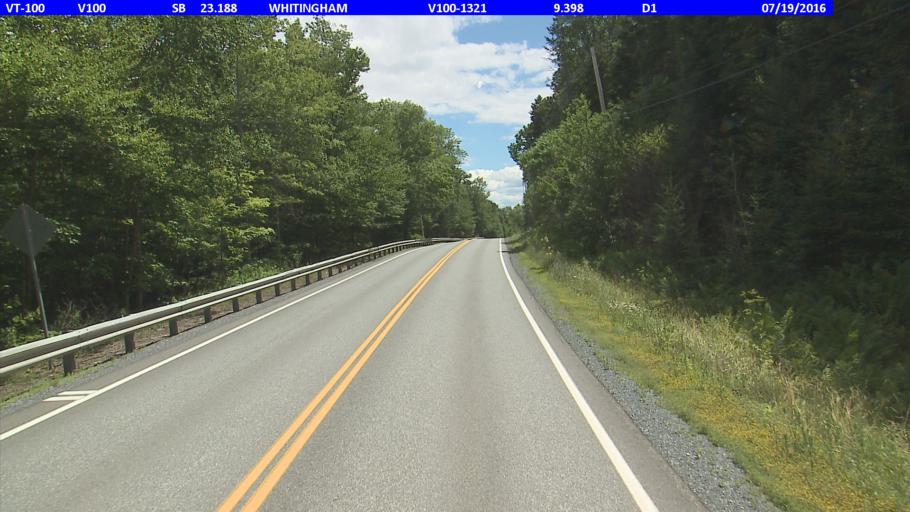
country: US
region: Vermont
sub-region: Windham County
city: Dover
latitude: 42.8139
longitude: -72.8451
